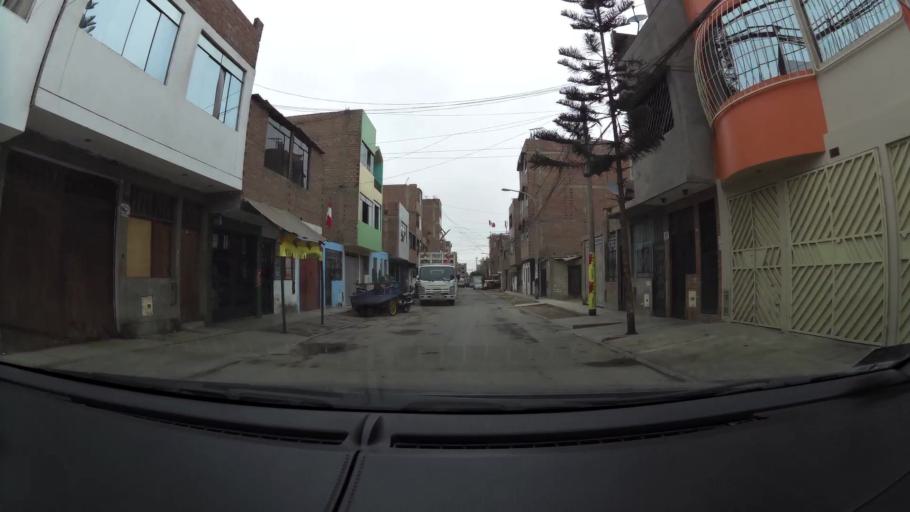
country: PE
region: Lima
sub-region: Lima
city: Independencia
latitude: -11.9680
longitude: -77.0787
